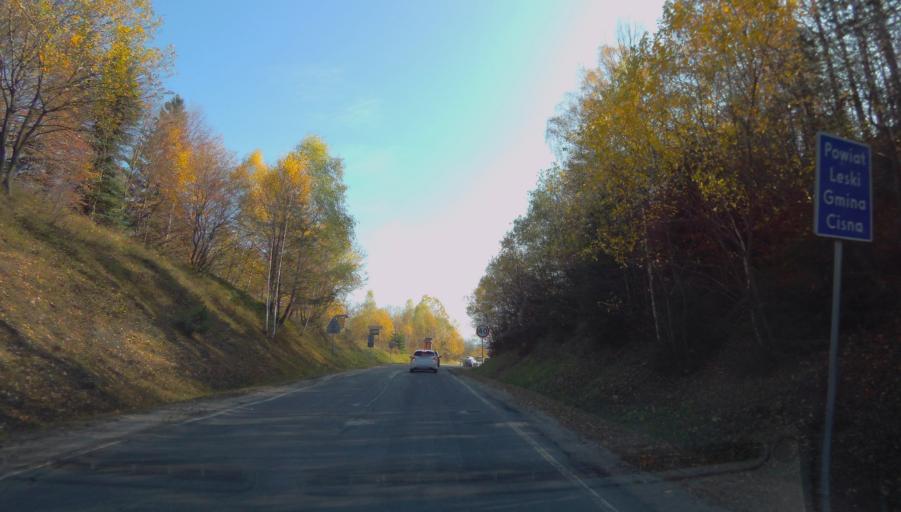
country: PL
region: Subcarpathian Voivodeship
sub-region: Powiat leski
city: Cisna
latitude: 49.2106
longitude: 22.2416
